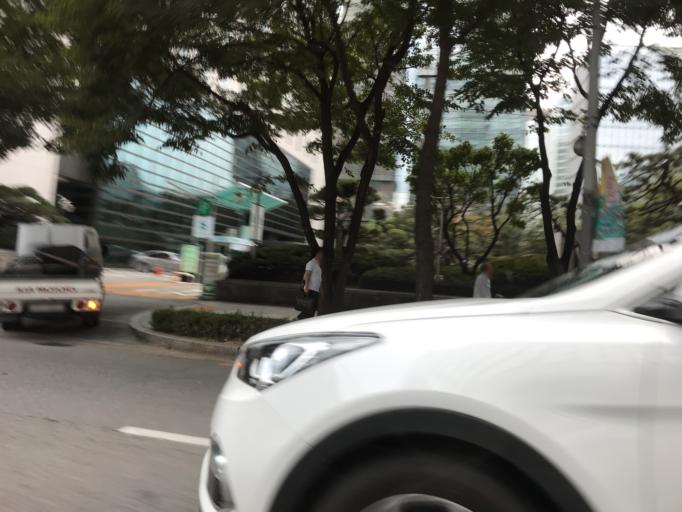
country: KR
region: Seoul
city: Seoul
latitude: 37.5716
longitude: 126.9830
